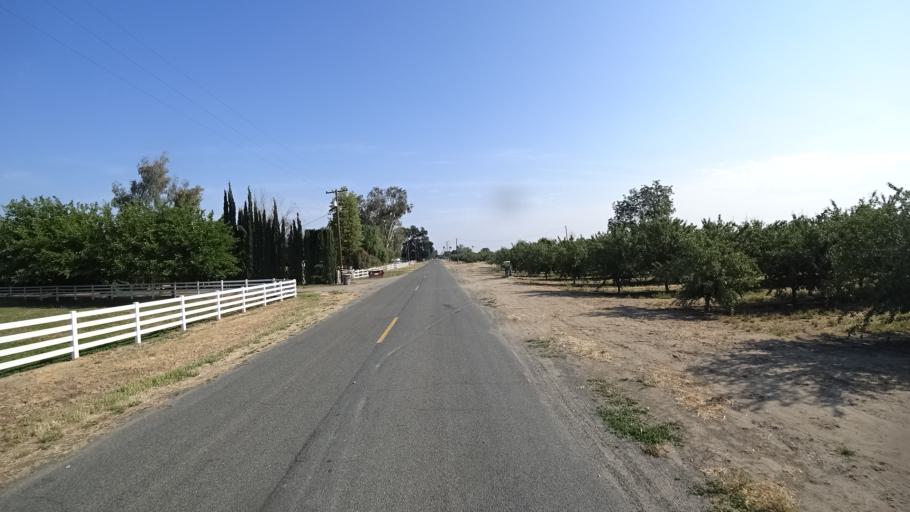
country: US
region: California
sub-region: Kings County
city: Lemoore
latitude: 36.3626
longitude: -119.8251
